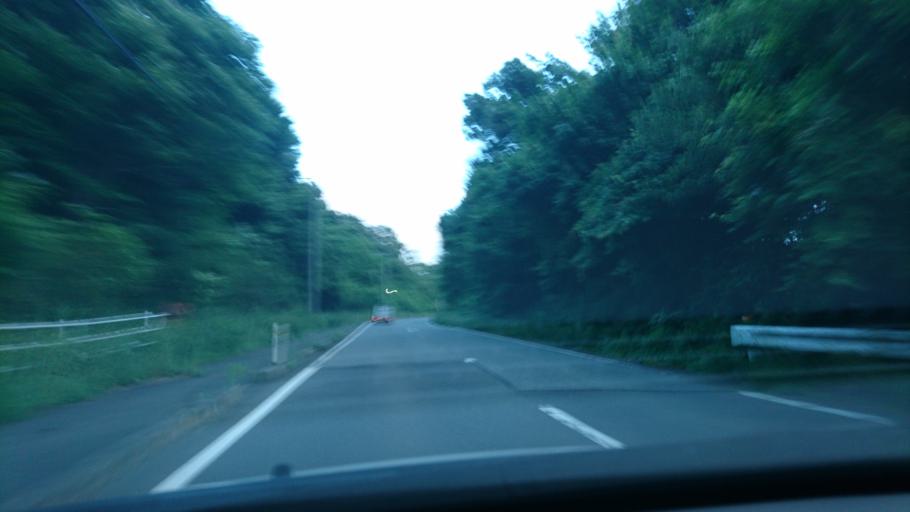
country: JP
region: Iwate
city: Ichinoseki
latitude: 38.7902
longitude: 141.0554
